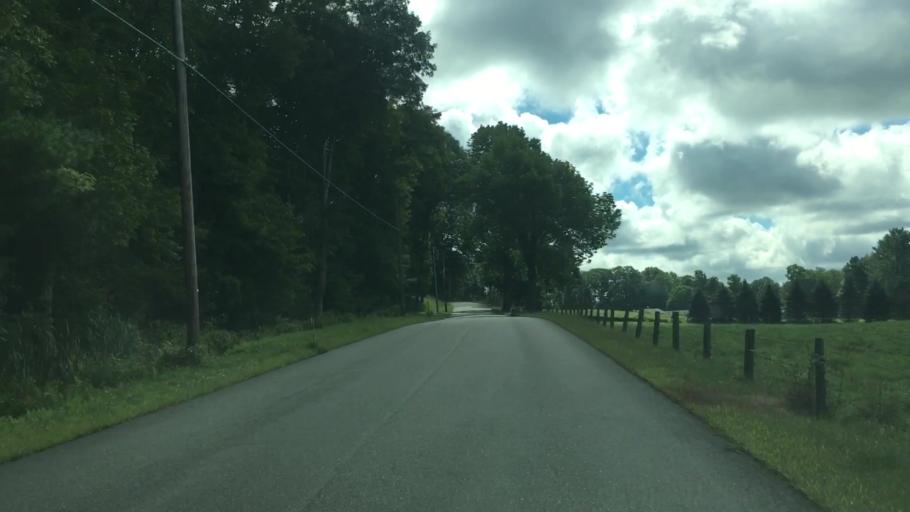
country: US
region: Connecticut
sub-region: Tolland County
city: Stafford Springs
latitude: 41.9234
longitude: -72.2392
